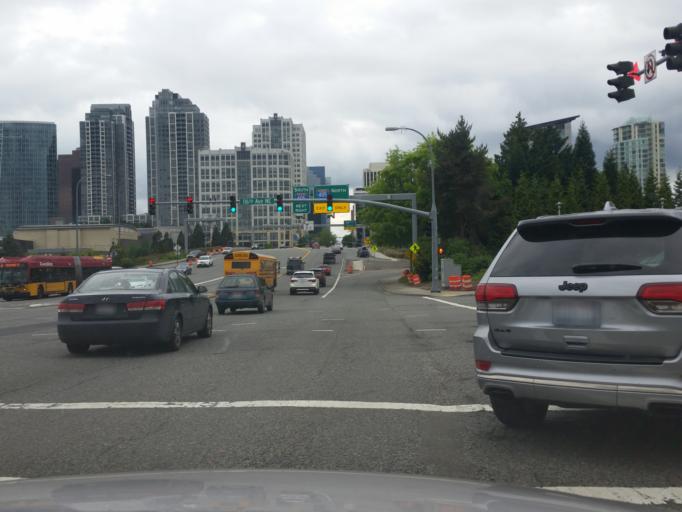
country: US
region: Washington
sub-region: King County
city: Bellevue
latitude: 47.6174
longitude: -122.1859
